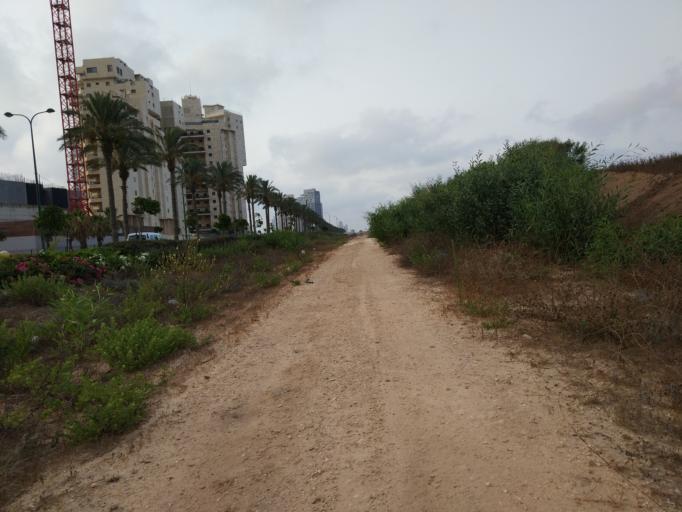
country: IL
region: Central District
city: Netanya
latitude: 32.3073
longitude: 34.8467
